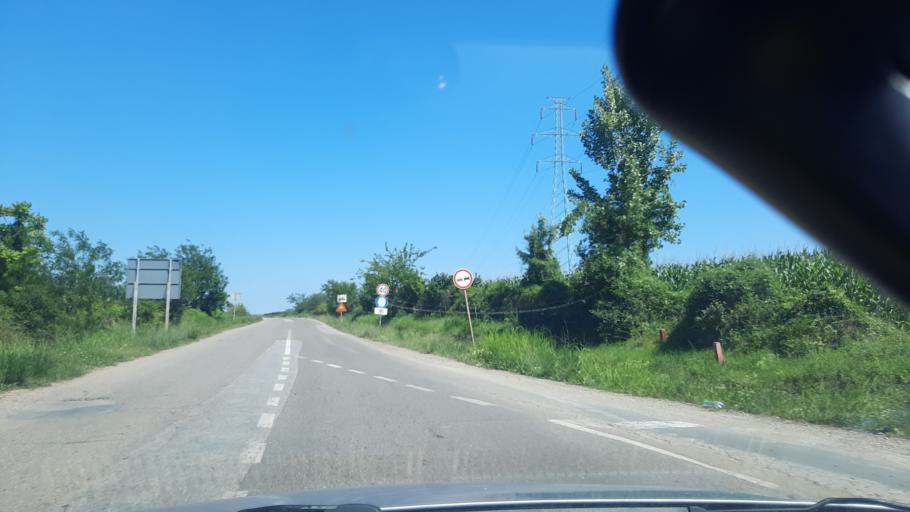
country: RS
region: Central Serbia
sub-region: Podunavski Okrug
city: Smederevo
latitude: 44.5887
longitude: 20.9735
